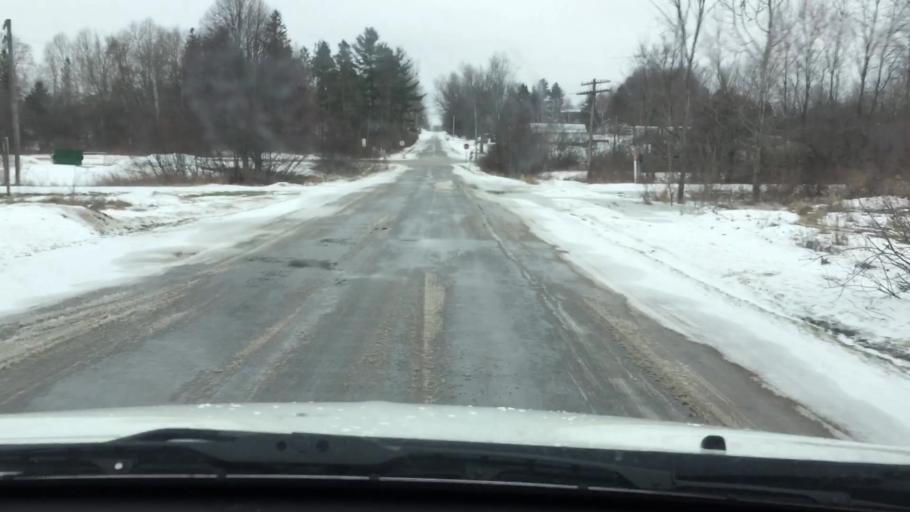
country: US
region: Michigan
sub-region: Osceola County
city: Reed City
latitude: 44.0372
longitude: -85.4538
